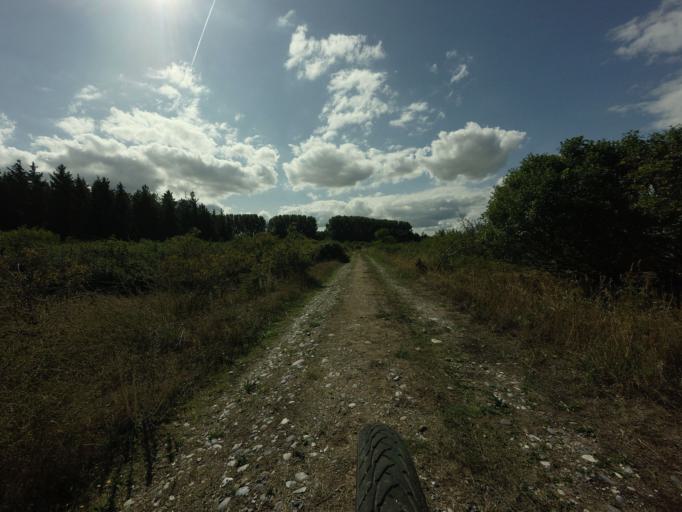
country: DK
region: Zealand
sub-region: Vordingborg Kommune
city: Stege
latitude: 55.0233
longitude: 12.4316
